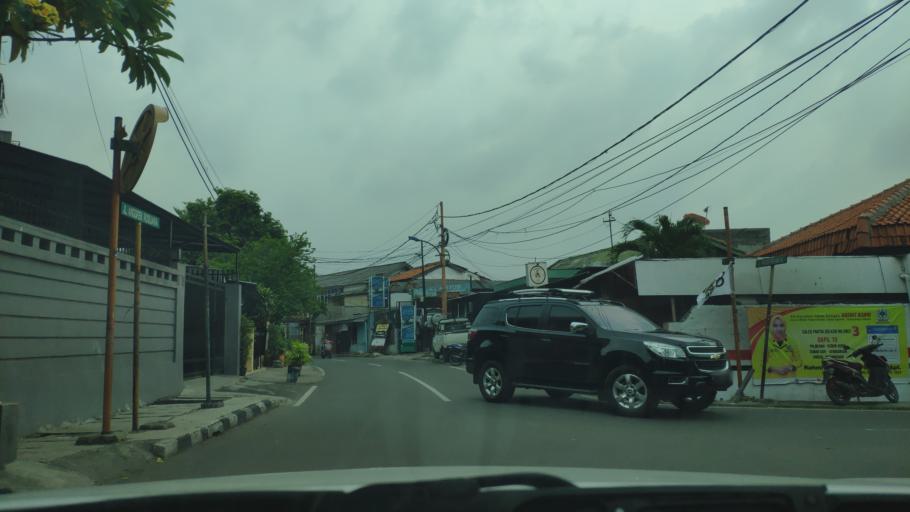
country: ID
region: Jakarta Raya
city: Jakarta
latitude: -6.1942
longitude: 106.7933
